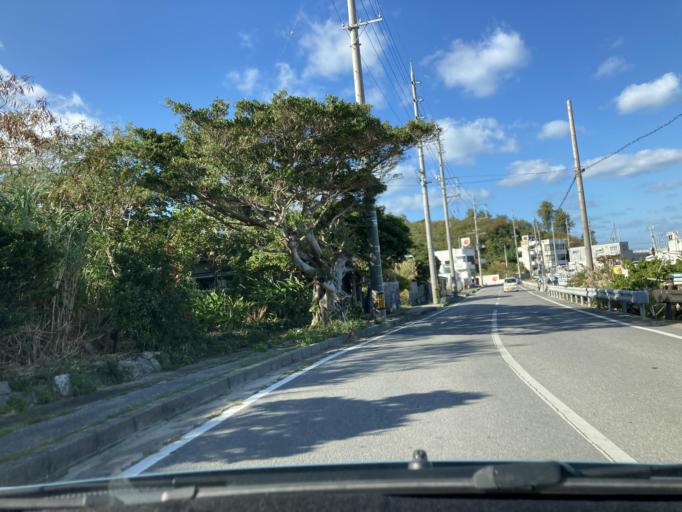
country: JP
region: Okinawa
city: Katsuren-haebaru
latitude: 26.3194
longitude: 127.9155
